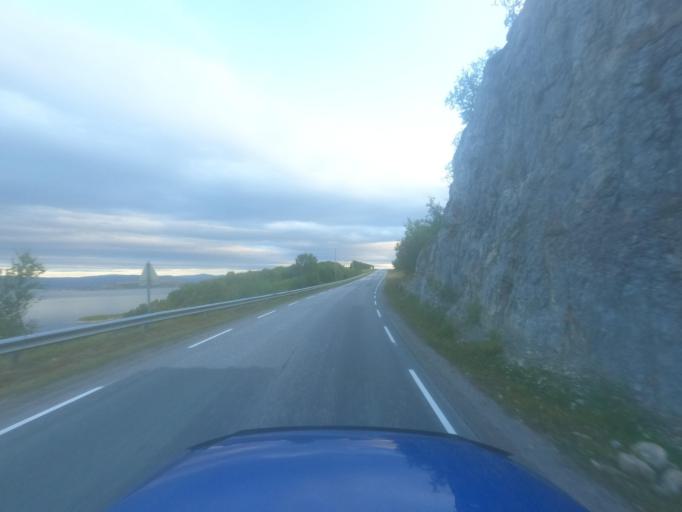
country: NO
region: Finnmark Fylke
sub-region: Porsanger
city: Lakselv
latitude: 70.2633
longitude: 25.0273
